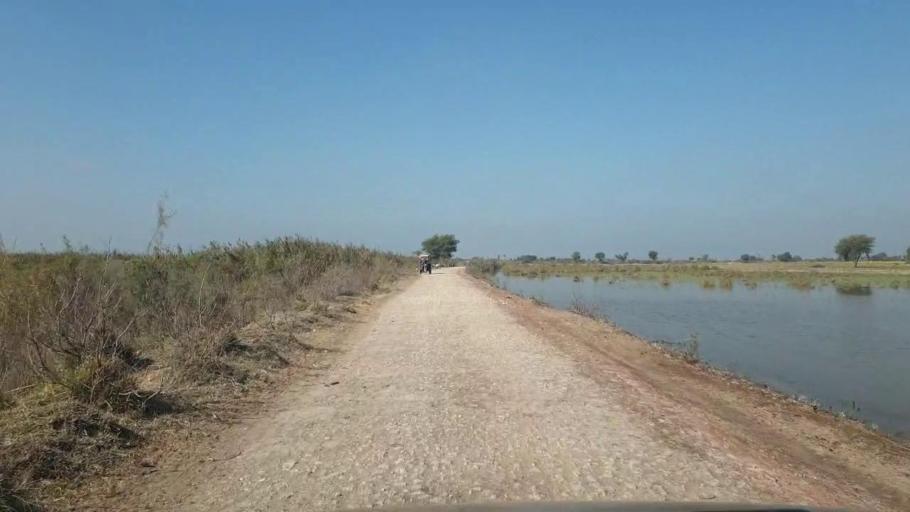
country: PK
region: Sindh
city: Bhit Shah
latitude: 25.8748
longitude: 68.5292
